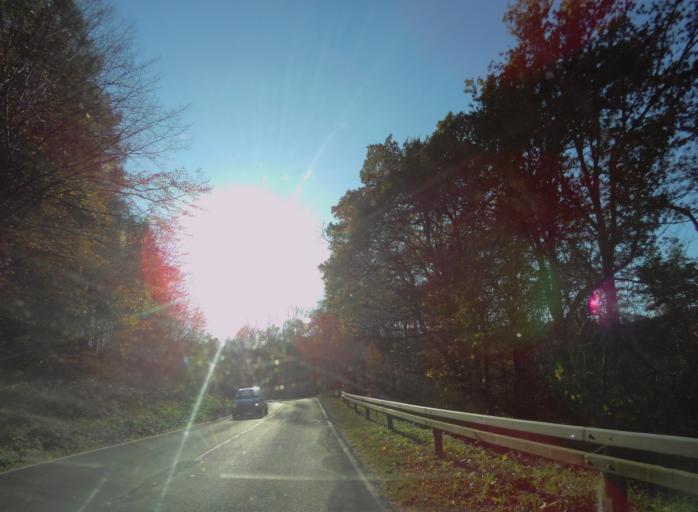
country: PL
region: Subcarpathian Voivodeship
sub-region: Powiat leski
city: Polanczyk
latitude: 49.3971
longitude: 22.4394
